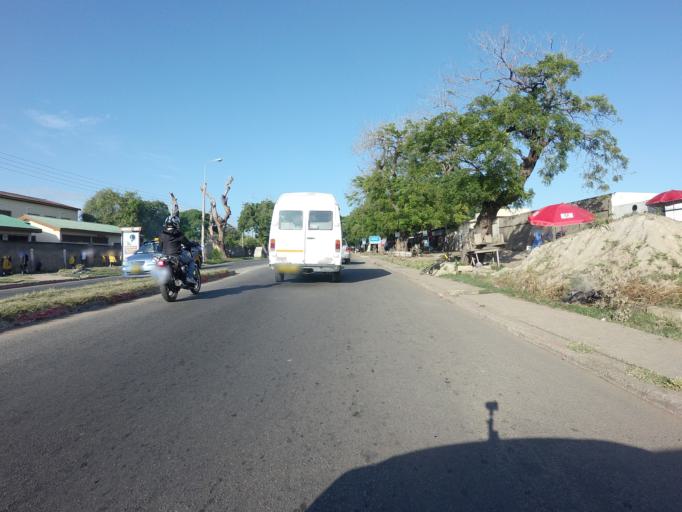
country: GH
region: Greater Accra
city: Accra
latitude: 5.5370
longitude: -0.2226
